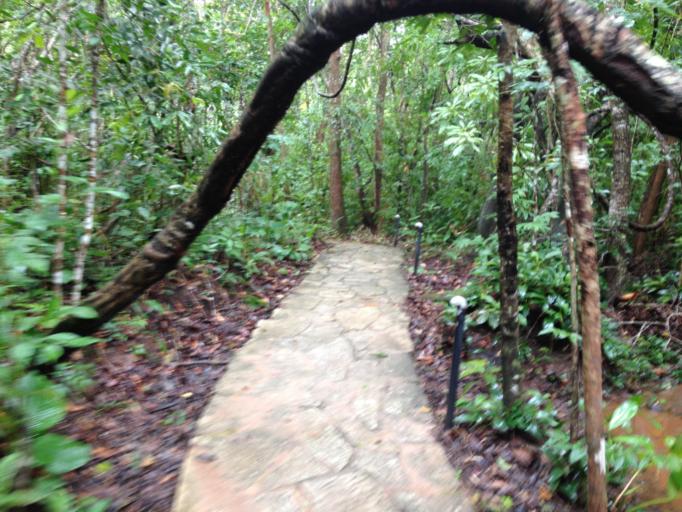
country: BR
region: Goias
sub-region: Niquelandia
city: Niquelandia
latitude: -14.2328
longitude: -47.9257
